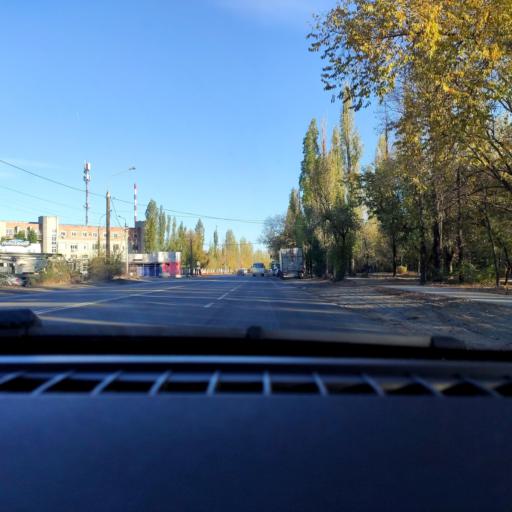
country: RU
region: Voronezj
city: Voronezh
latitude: 51.6363
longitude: 39.2640
